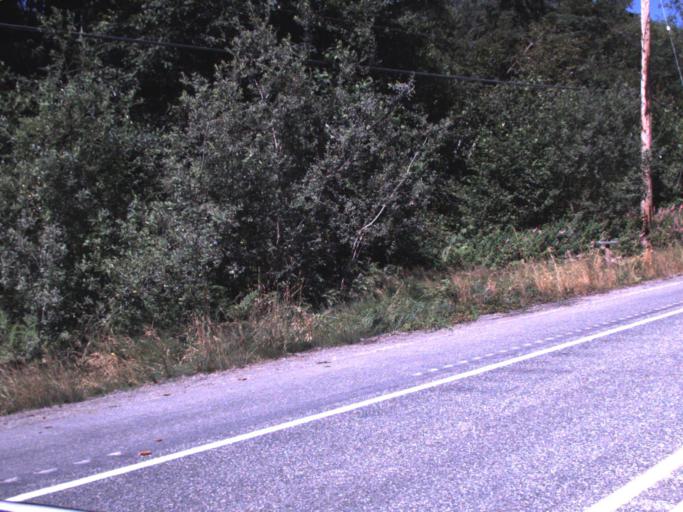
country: US
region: Washington
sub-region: King County
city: Enumclaw
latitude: 47.1796
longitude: -121.9205
